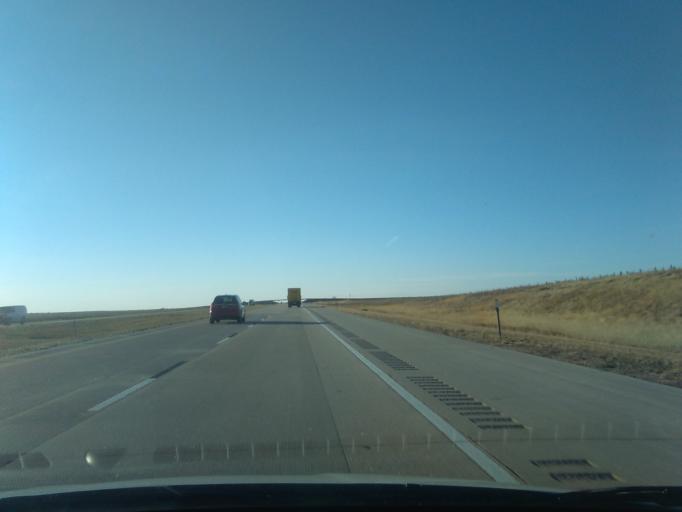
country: US
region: Nebraska
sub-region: Deuel County
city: Chappell
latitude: 41.1134
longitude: -102.7070
